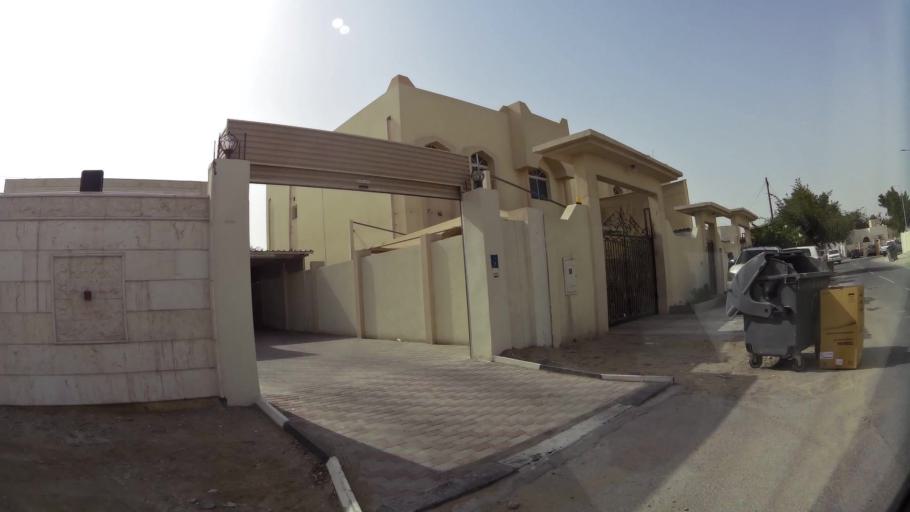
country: QA
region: Baladiyat ar Rayyan
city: Ar Rayyan
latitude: 25.2508
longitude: 51.4407
